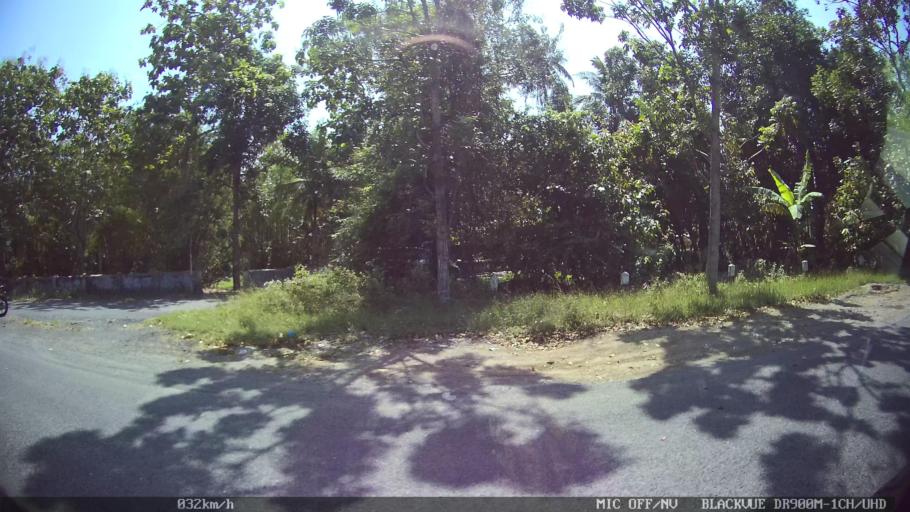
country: ID
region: Daerah Istimewa Yogyakarta
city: Srandakan
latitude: -7.8857
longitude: 110.0456
